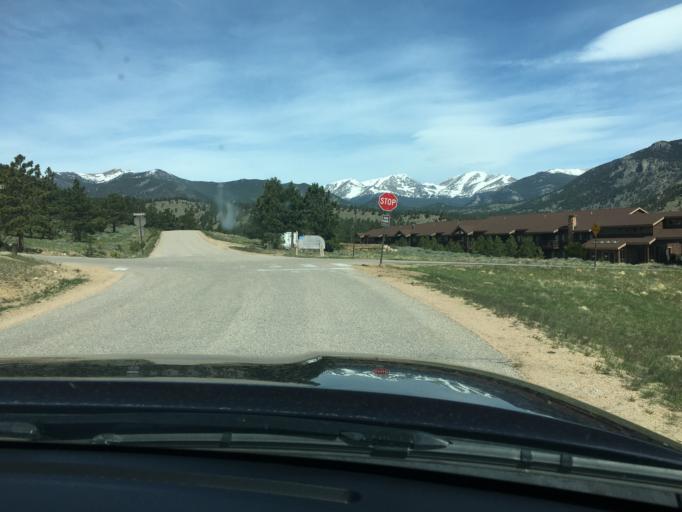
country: US
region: Colorado
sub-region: Larimer County
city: Estes Park
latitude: 40.3378
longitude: -105.5750
